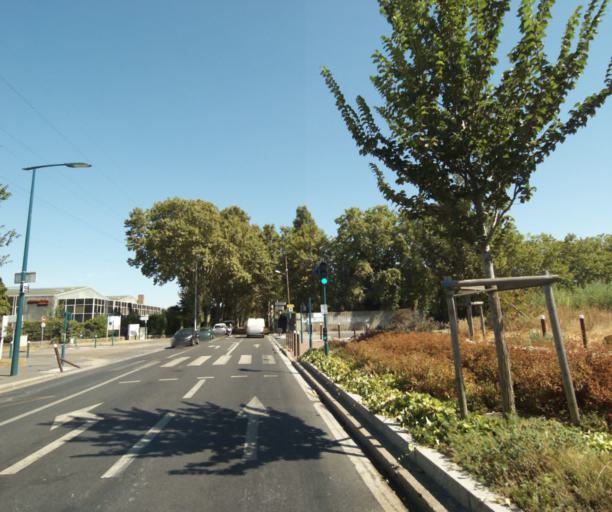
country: FR
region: Ile-de-France
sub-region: Departement des Hauts-de-Seine
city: Villeneuve-la-Garenne
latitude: 48.9449
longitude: 2.3100
